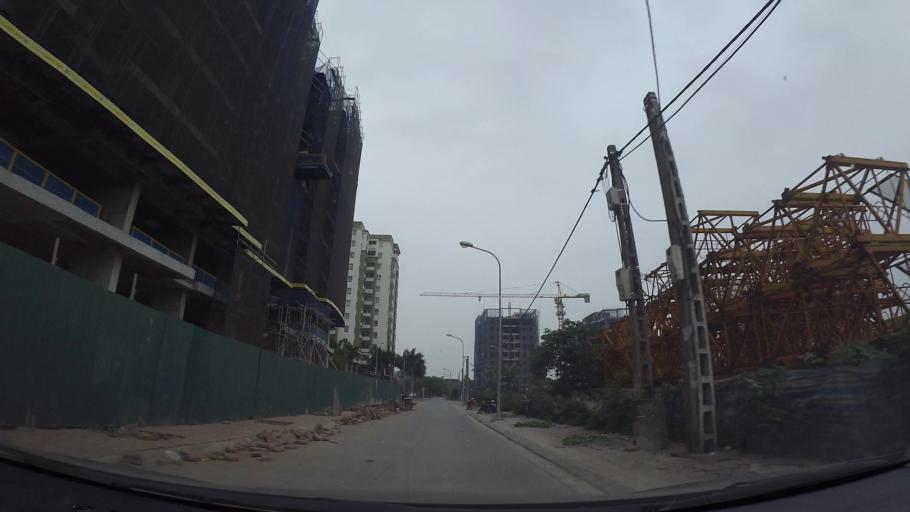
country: VN
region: Ha Noi
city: Trau Quy
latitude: 21.0379
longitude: 105.9086
